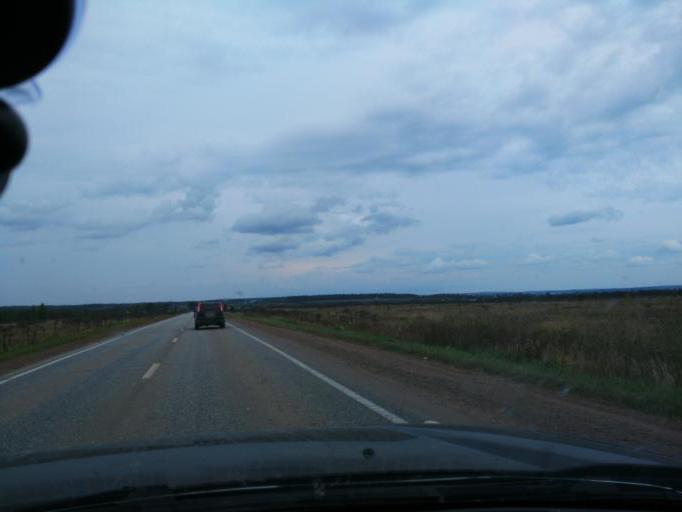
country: RU
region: Perm
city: Chernushka
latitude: 56.5063
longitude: 55.9951
